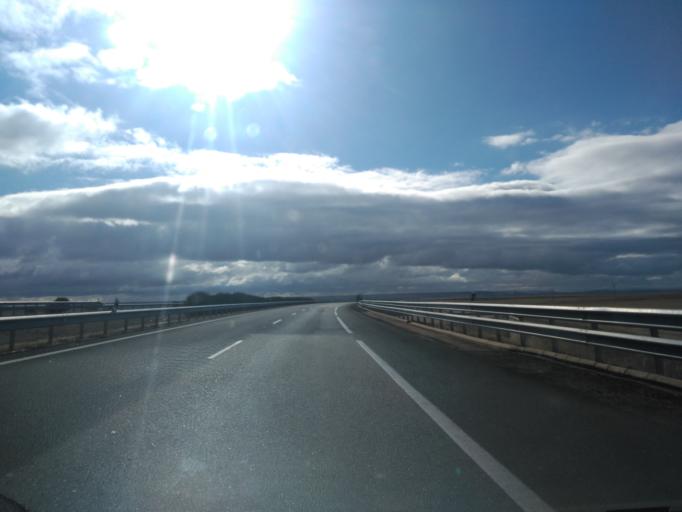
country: ES
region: Castille and Leon
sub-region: Provincia de Palencia
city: Marcilla de Campos
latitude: 42.3058
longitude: -4.3988
